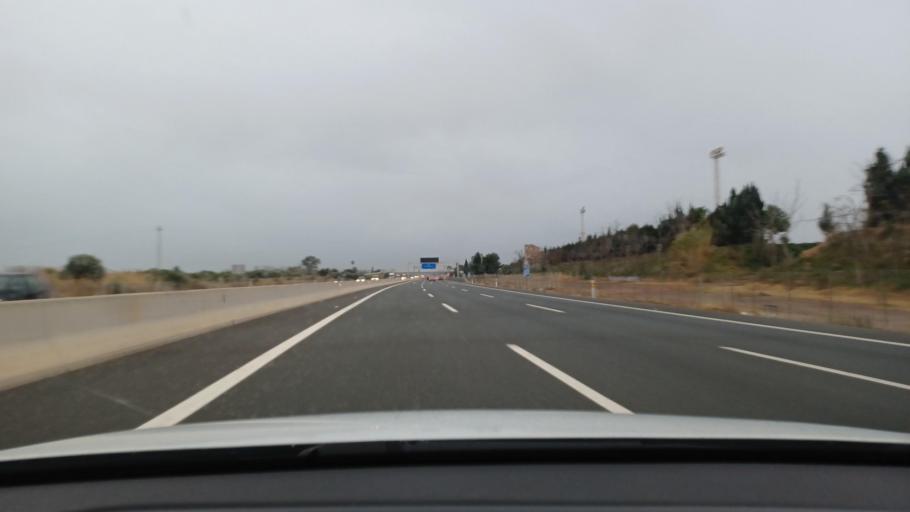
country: ES
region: Valencia
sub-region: Provincia de Valencia
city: Puig
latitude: 39.5935
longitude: -0.2932
